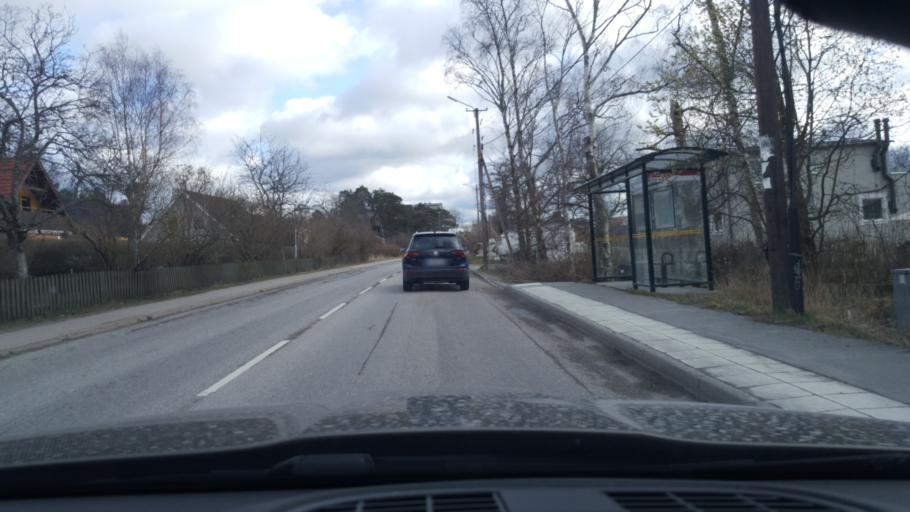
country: SE
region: Stockholm
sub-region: Osterakers Kommun
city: Akersberga
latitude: 59.4853
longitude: 18.2911
